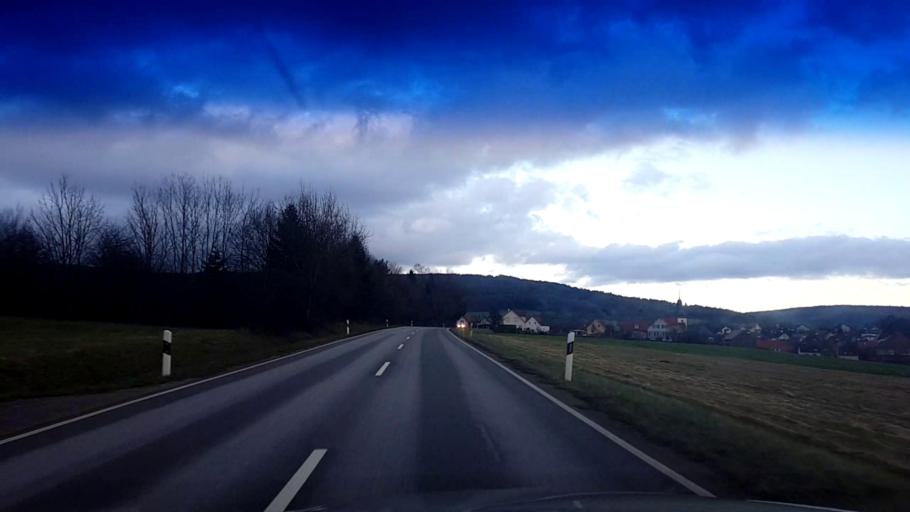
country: DE
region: Bavaria
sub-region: Upper Franconia
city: Buttenheim
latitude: 49.8096
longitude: 11.0704
